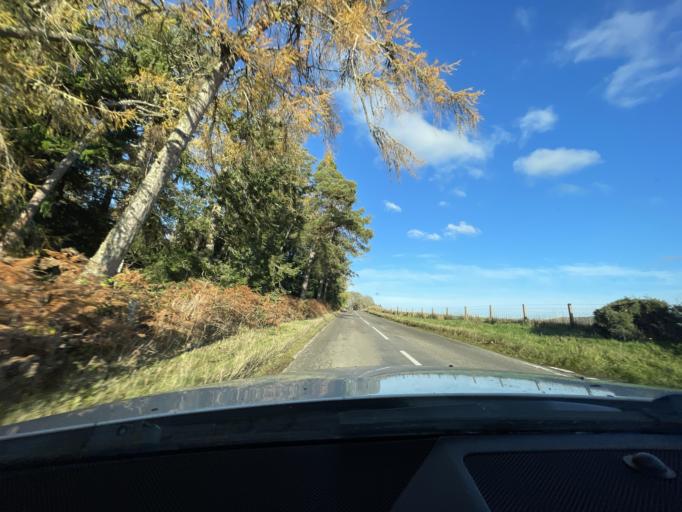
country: GB
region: Scotland
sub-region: Highland
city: Inverness
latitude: 57.4008
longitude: -4.3182
